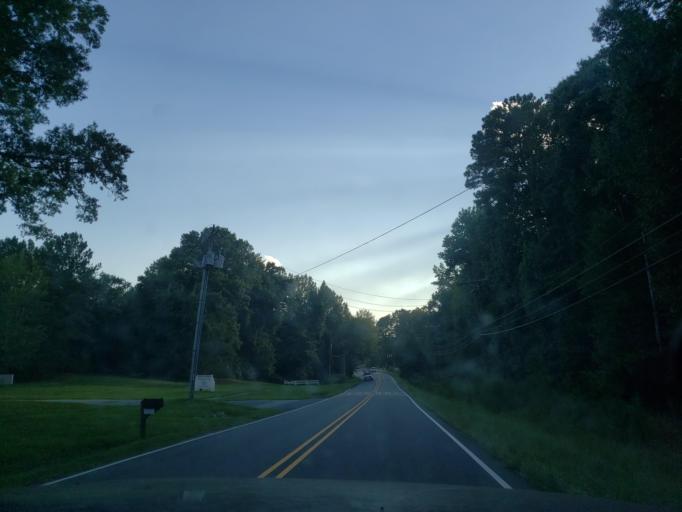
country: US
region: North Carolina
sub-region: Durham County
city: Durham
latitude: 35.9907
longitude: -78.9864
